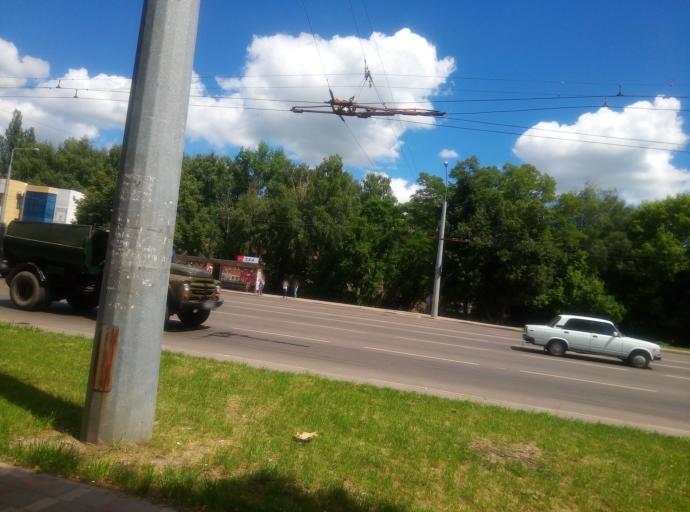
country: RU
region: Kursk
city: Kursk
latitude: 51.7664
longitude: 36.1829
